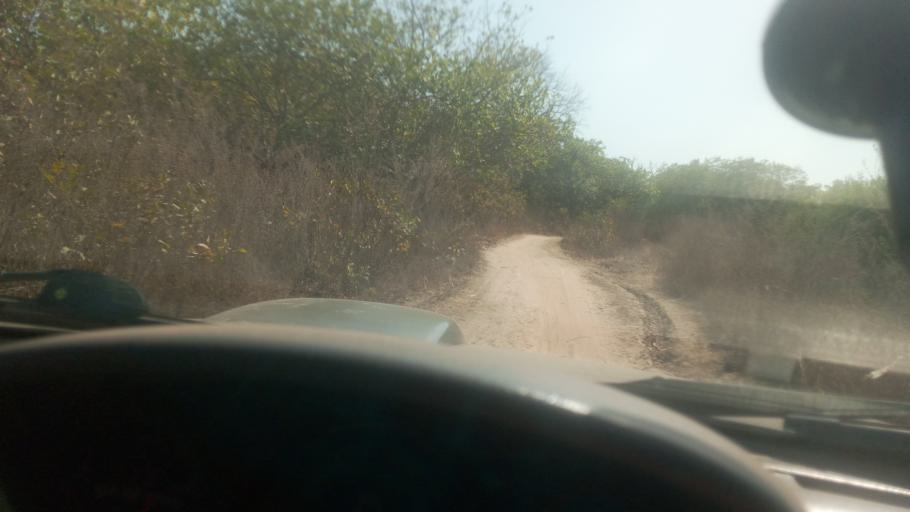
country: GW
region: Oio
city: Farim
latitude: 12.4497
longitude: -15.4273
